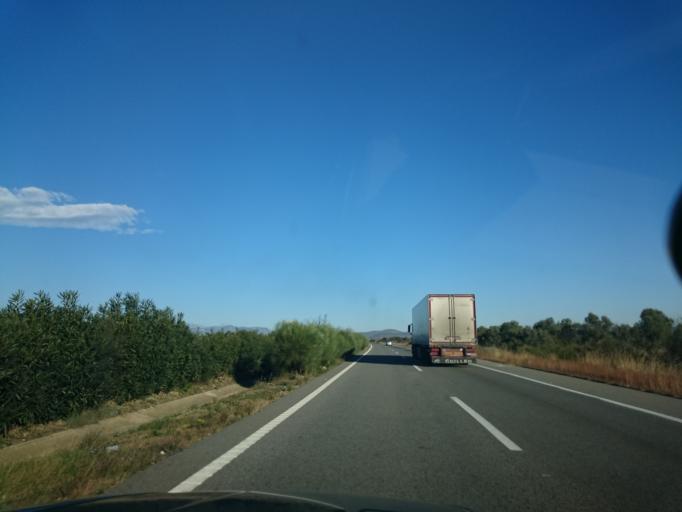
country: ES
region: Catalonia
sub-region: Provincia de Tarragona
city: Alcanar
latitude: 40.5308
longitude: 0.4185
